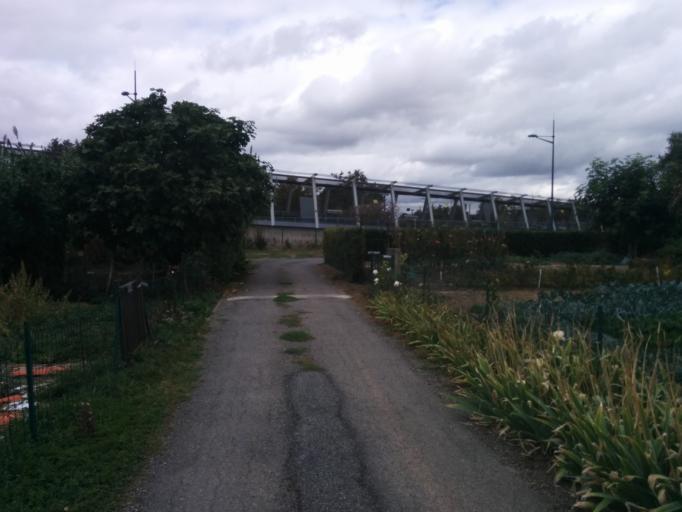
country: FR
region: Midi-Pyrenees
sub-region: Departement de la Haute-Garonne
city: Balma
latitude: 43.6261
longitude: 1.4821
